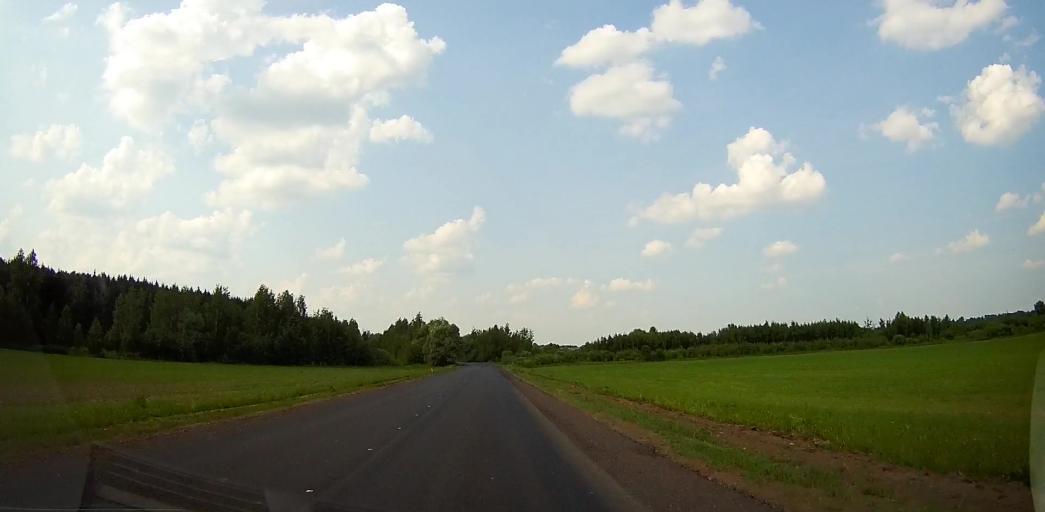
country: RU
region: Moskovskaya
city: Malino
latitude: 55.0608
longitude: 38.1362
